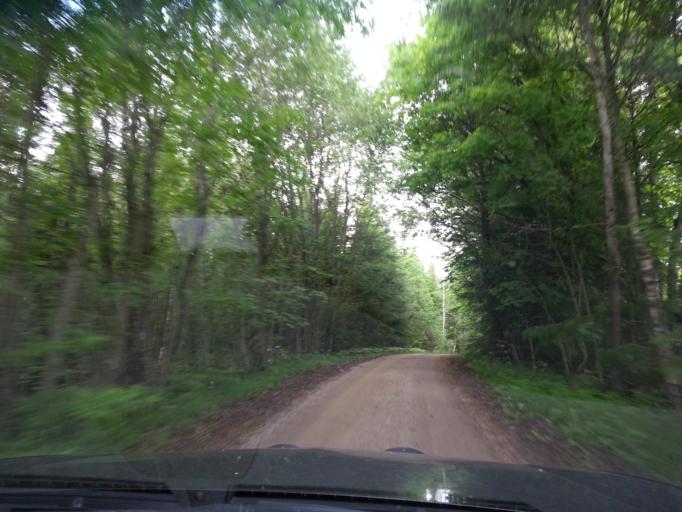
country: SE
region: Joenkoeping
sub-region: Vetlanda Kommun
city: Vetlanda
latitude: 57.2861
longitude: 15.1283
